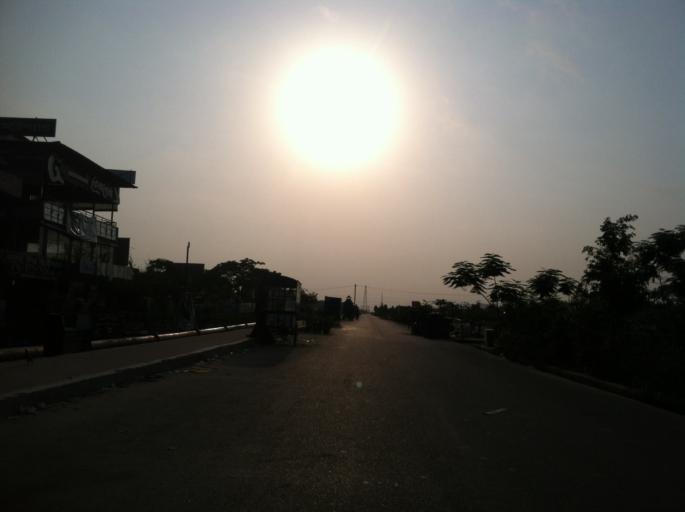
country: BD
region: Dhaka
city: Tungi
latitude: 23.8273
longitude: 90.4313
